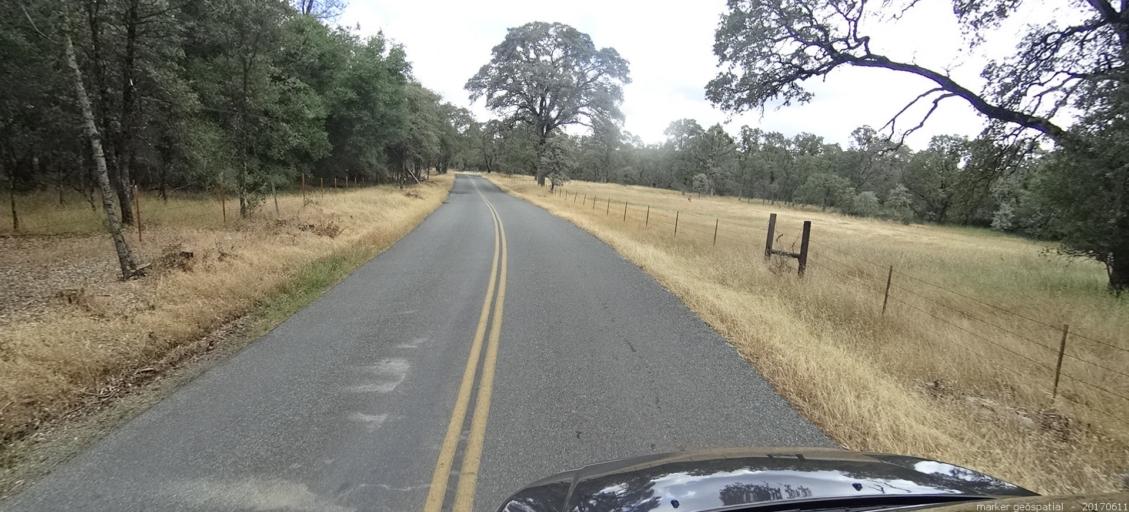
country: US
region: California
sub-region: Butte County
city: Oroville
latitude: 39.6206
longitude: -121.5274
